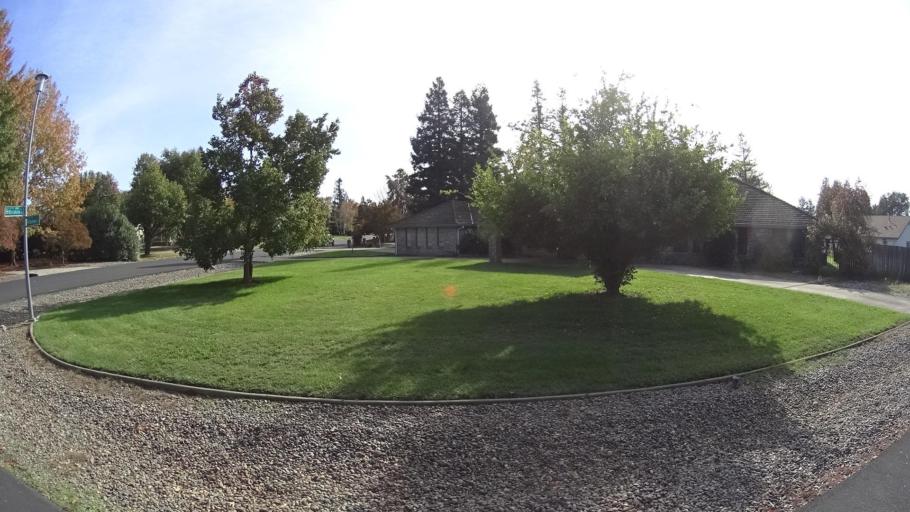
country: US
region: California
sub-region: Sacramento County
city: Vineyard
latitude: 38.4403
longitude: -121.3642
